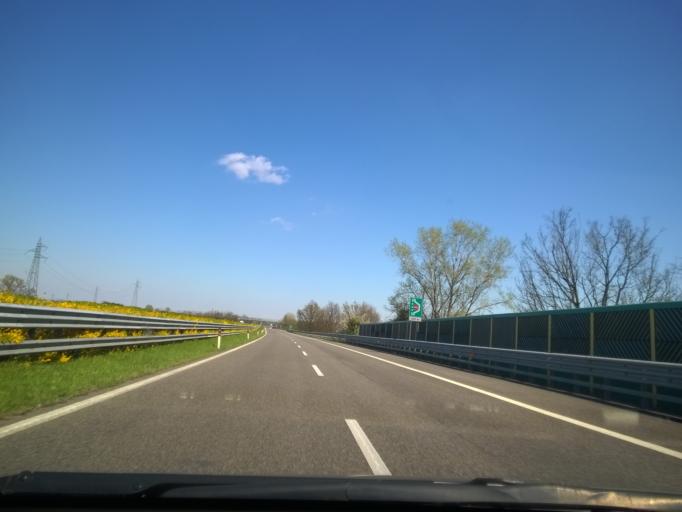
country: IT
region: Emilia-Romagna
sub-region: Provincia di Piacenza
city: Pontenure
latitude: 45.0445
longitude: 9.8142
